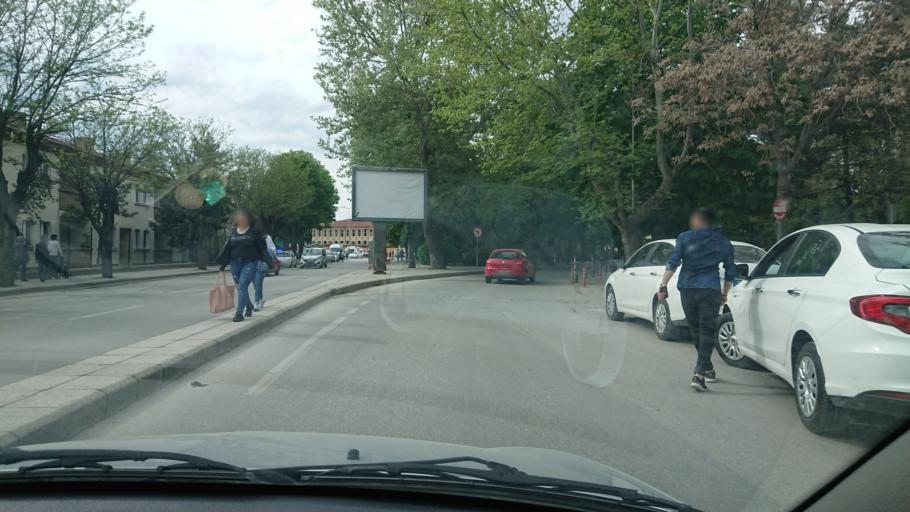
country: TR
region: Eskisehir
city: Eskisehir
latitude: 39.7781
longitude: 30.5085
